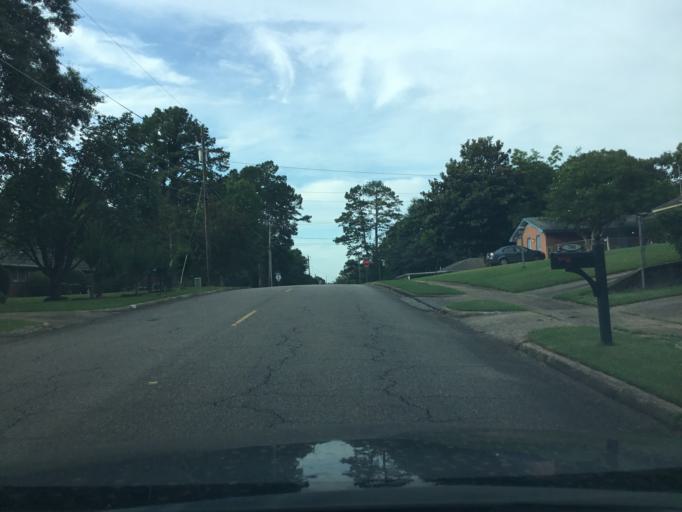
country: US
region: Alabama
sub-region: Montgomery County
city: Montgomery
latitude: 32.3718
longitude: -86.2555
